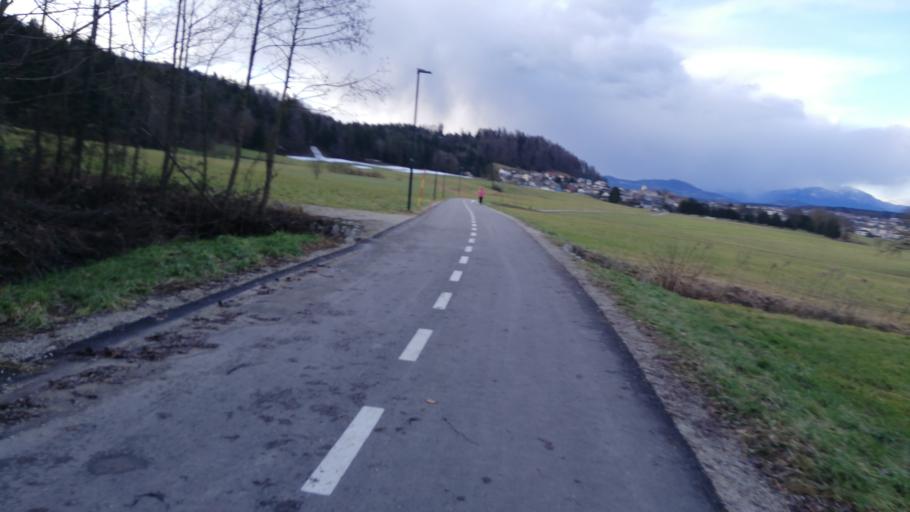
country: SI
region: Medvode
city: Medvode
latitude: 46.1244
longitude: 14.4194
